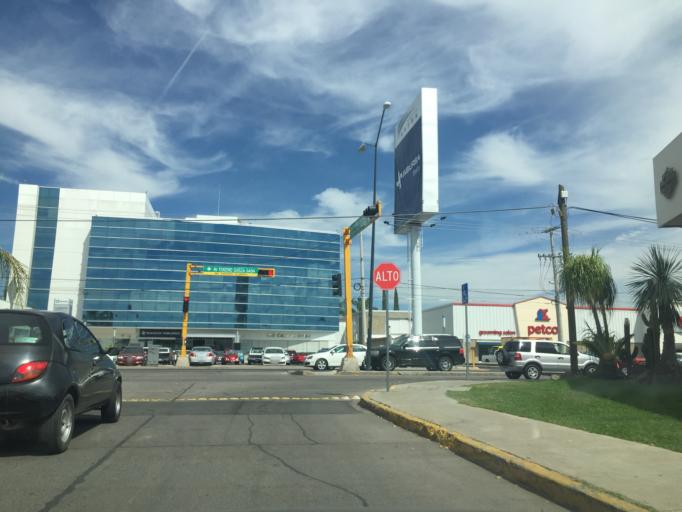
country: MX
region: Guanajuato
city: Leon
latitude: 21.1609
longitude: -101.6938
